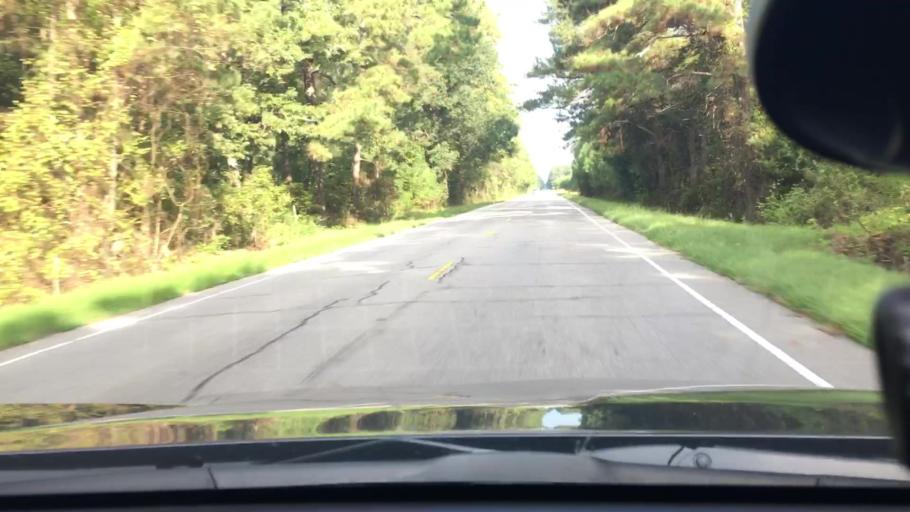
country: US
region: North Carolina
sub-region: Edgecombe County
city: Pinetops
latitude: 35.7575
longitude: -77.5523
